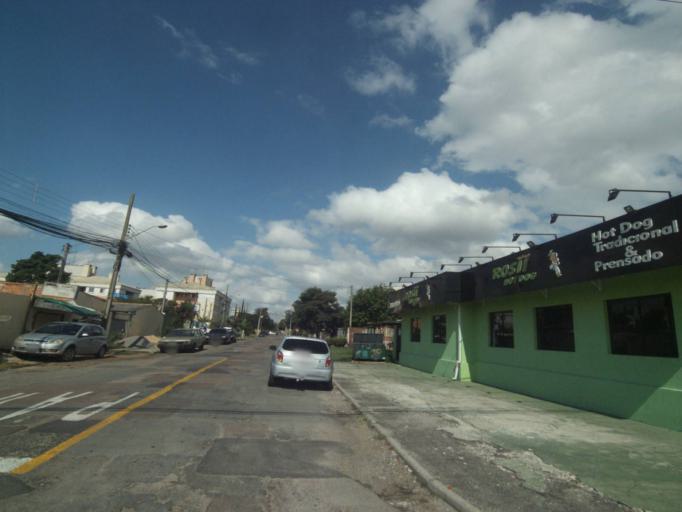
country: BR
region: Parana
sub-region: Curitiba
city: Curitiba
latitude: -25.4956
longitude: -49.3092
